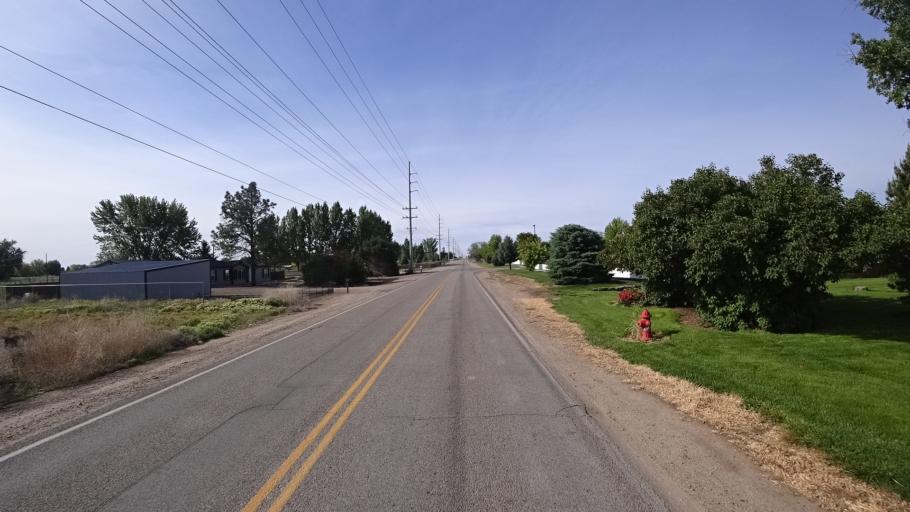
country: US
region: Idaho
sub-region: Ada County
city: Kuna
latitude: 43.4819
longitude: -116.4137
